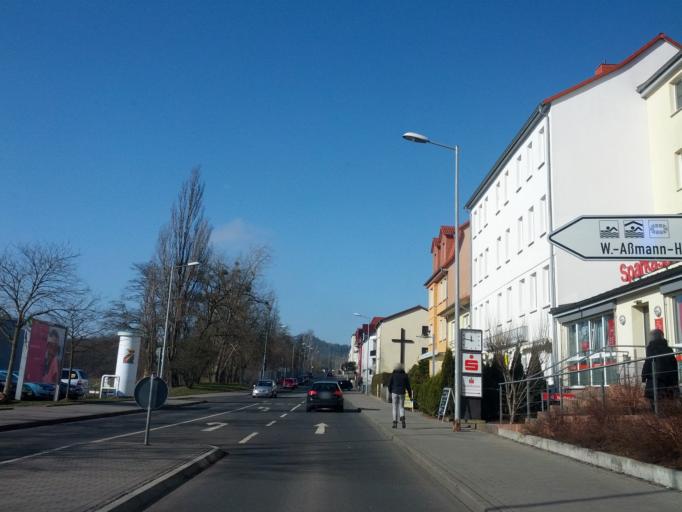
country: DE
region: Thuringia
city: Eisenach
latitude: 50.9850
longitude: 10.3128
